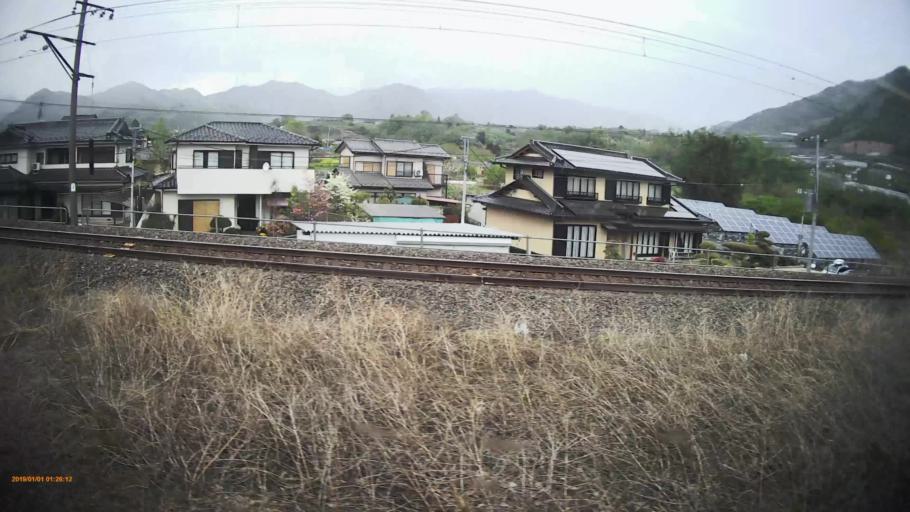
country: JP
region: Yamanashi
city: Enzan
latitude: 35.7046
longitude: 138.7404
